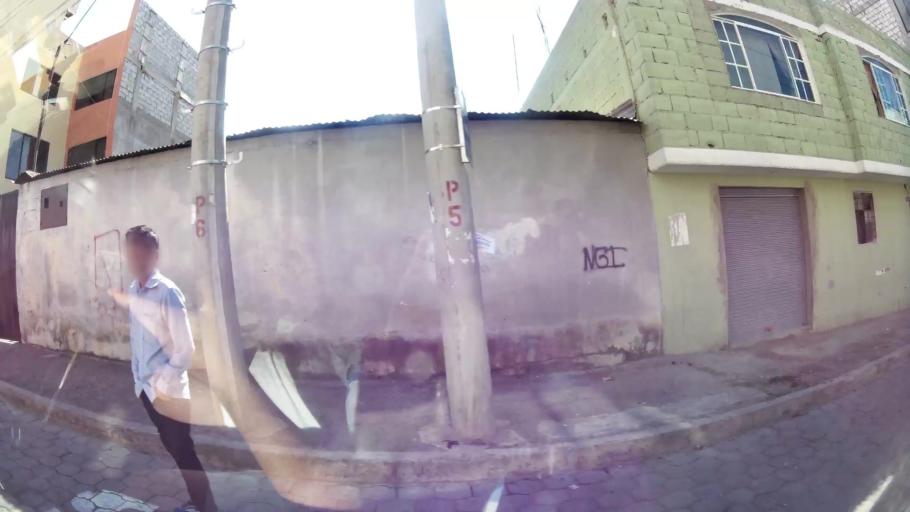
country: EC
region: Pichincha
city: Quito
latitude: -0.1224
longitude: -78.4708
